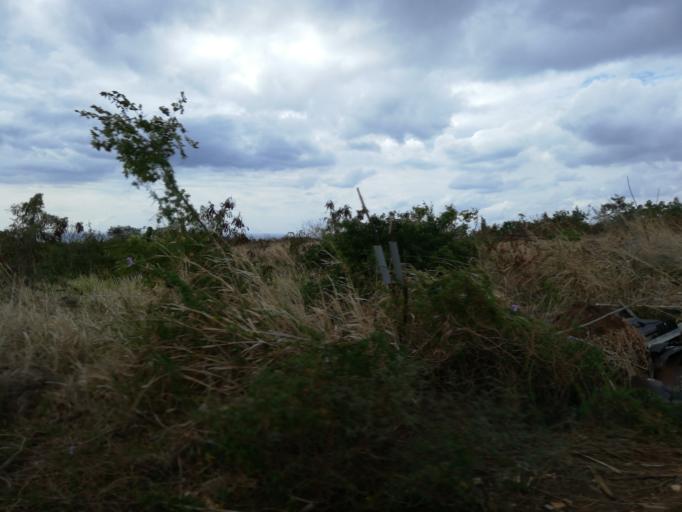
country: MU
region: Black River
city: Petite Riviere
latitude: -20.2085
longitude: 57.4597
